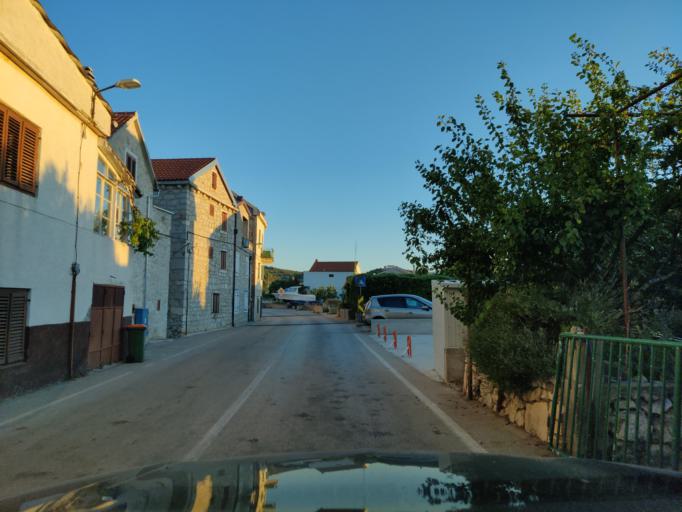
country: HR
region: Sibensko-Kniniska
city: Murter
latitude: 43.8225
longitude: 15.6032
